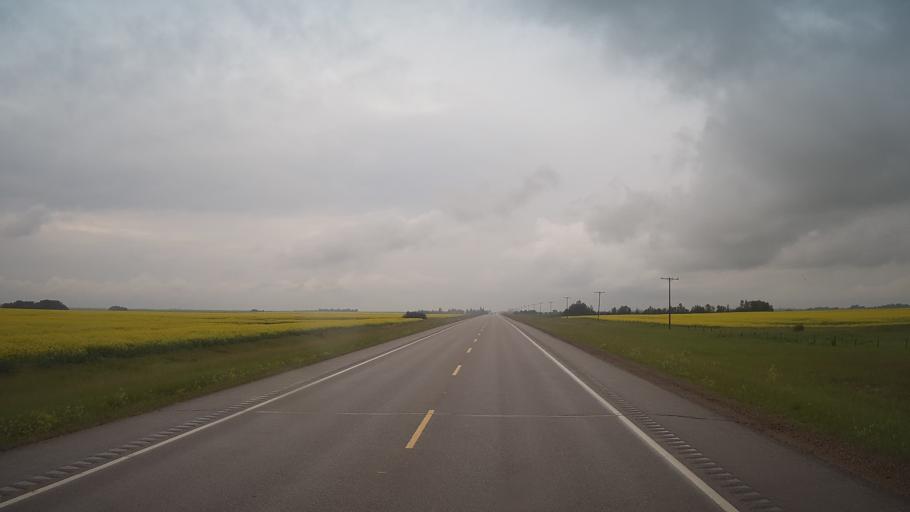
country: CA
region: Saskatchewan
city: Unity
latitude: 52.4349
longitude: -109.0061
